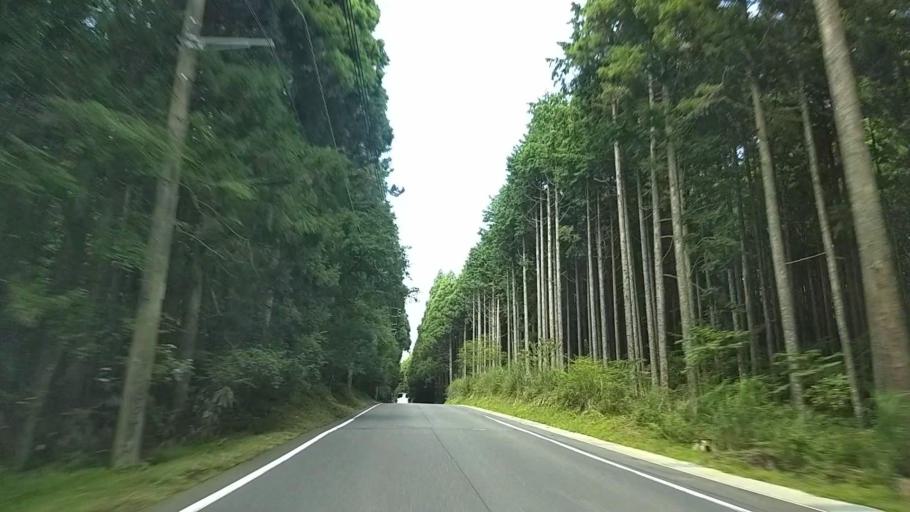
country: JP
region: Shizuoka
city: Gotemba
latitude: 35.2552
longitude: 138.8301
